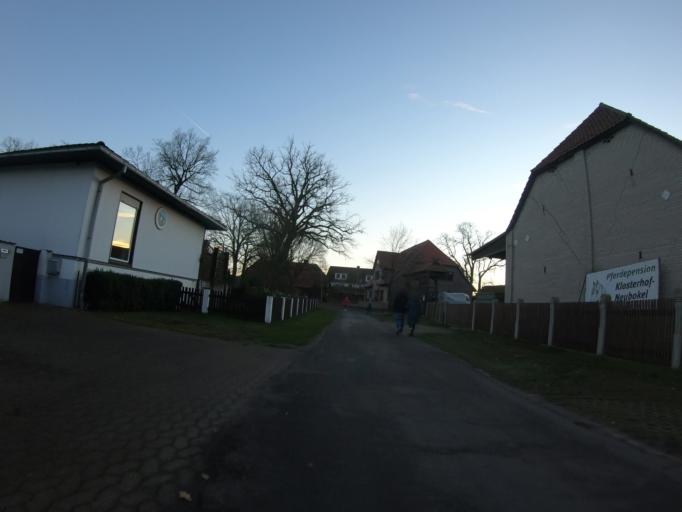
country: DE
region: Lower Saxony
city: Wagenhoff
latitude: 52.4913
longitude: 10.4726
